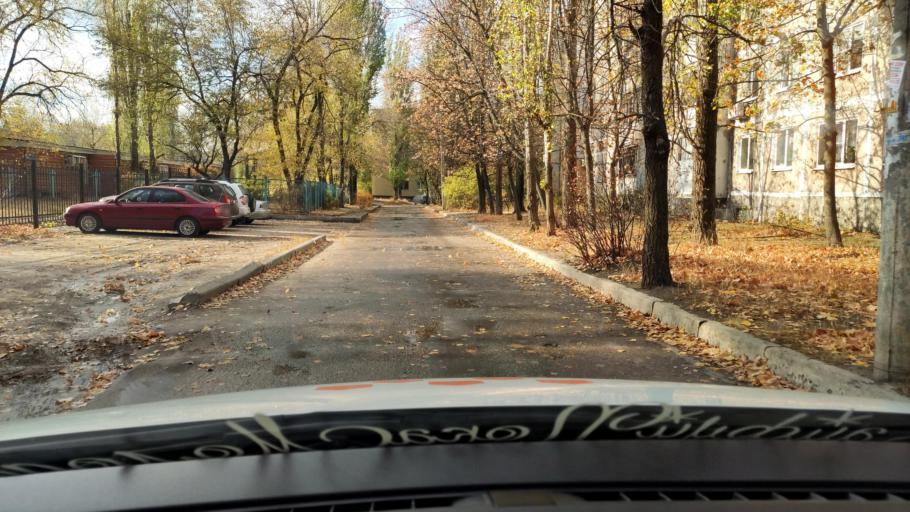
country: RU
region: Voronezj
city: Voronezh
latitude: 51.6495
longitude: 39.1312
